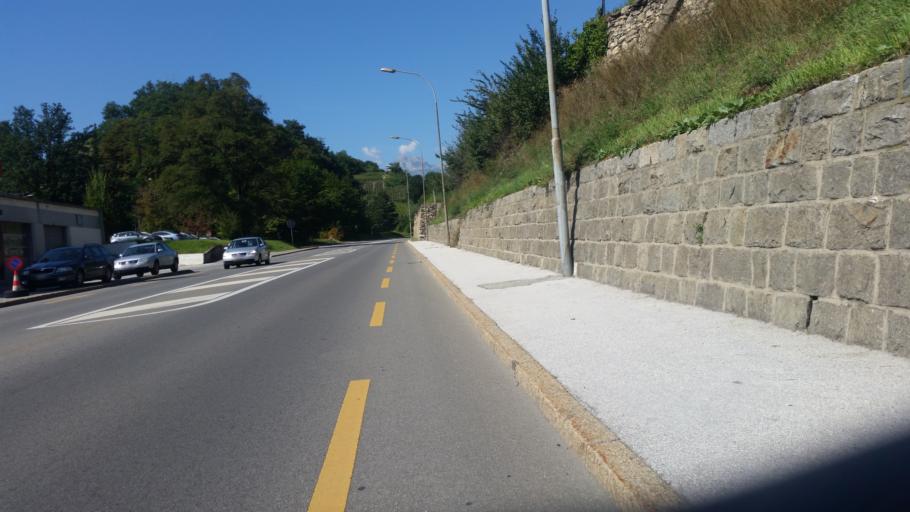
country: CH
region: Valais
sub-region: Sion District
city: Sitten
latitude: 46.2258
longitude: 7.3323
